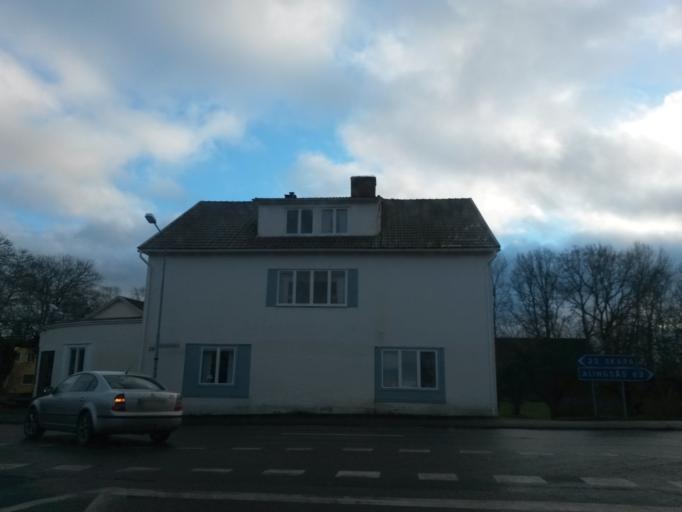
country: SE
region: Vaestra Goetaland
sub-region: Vara Kommun
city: Kvanum
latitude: 58.3245
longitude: 13.1040
